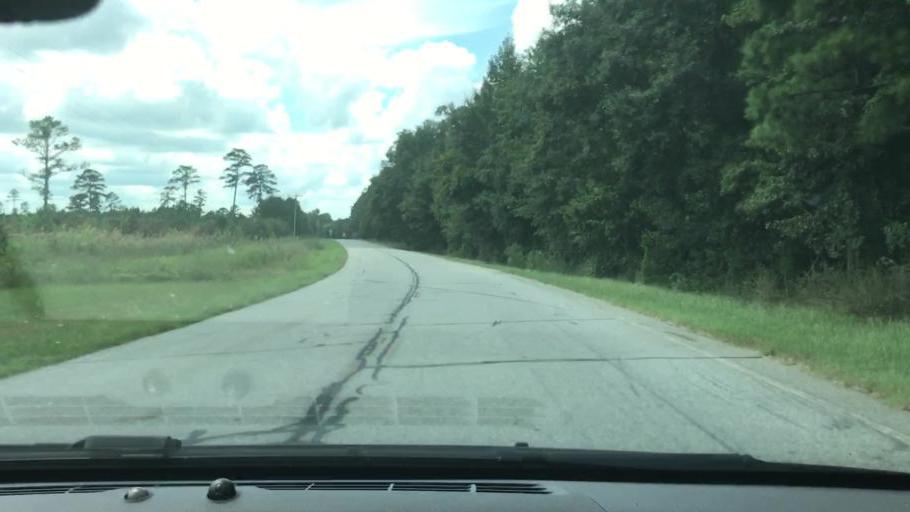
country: US
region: Georgia
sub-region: Stewart County
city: Lumpkin
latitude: 32.1433
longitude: -85.0190
